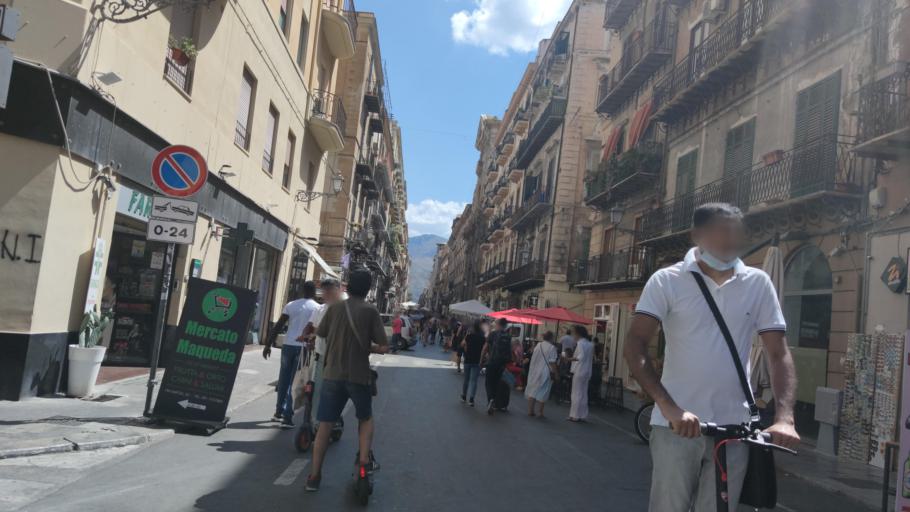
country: IT
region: Sicily
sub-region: Palermo
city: Palermo
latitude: 38.1175
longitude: 13.3603
